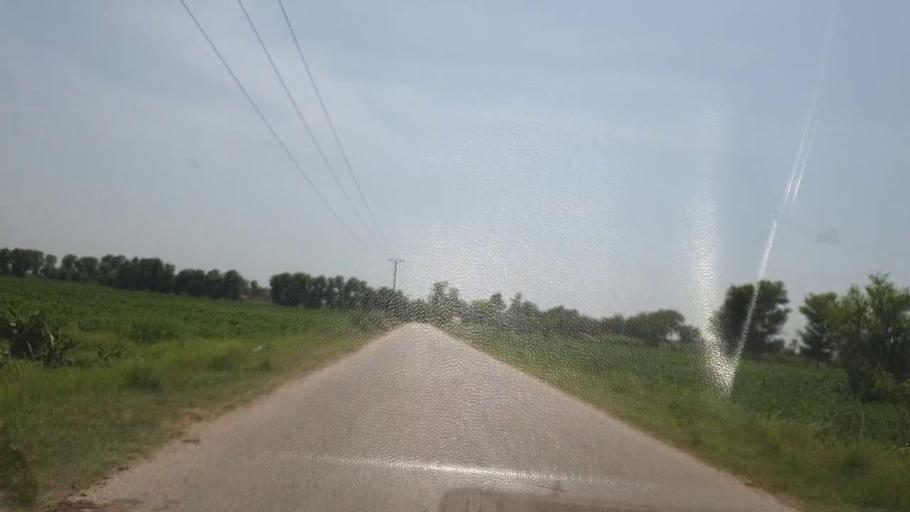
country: PK
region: Sindh
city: Bozdar
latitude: 27.0638
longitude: 68.5860
